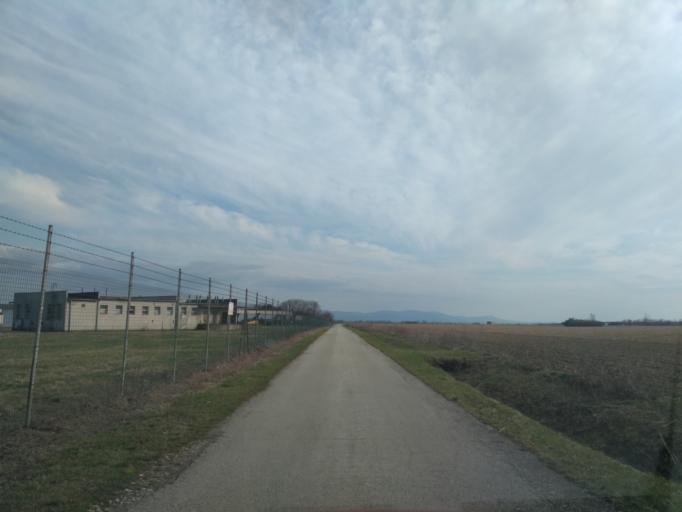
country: SK
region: Kosicky
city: Kosice
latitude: 48.6706
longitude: 21.2332
